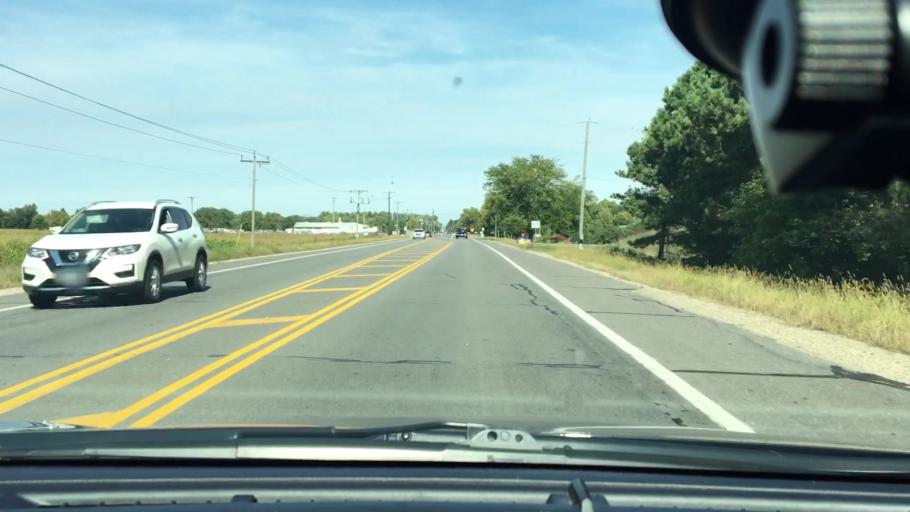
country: US
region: Minnesota
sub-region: Wright County
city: Saint Michael
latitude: 45.1936
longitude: -93.6650
